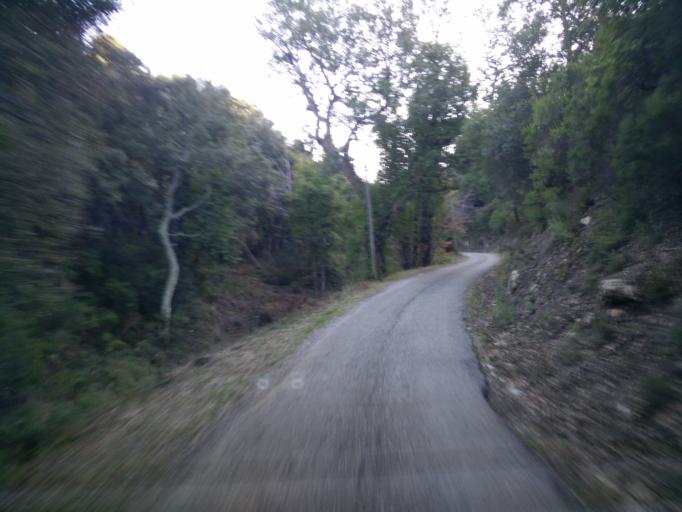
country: FR
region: Provence-Alpes-Cote d'Azur
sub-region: Departement du Var
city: Collobrieres
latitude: 43.2566
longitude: 6.3067
